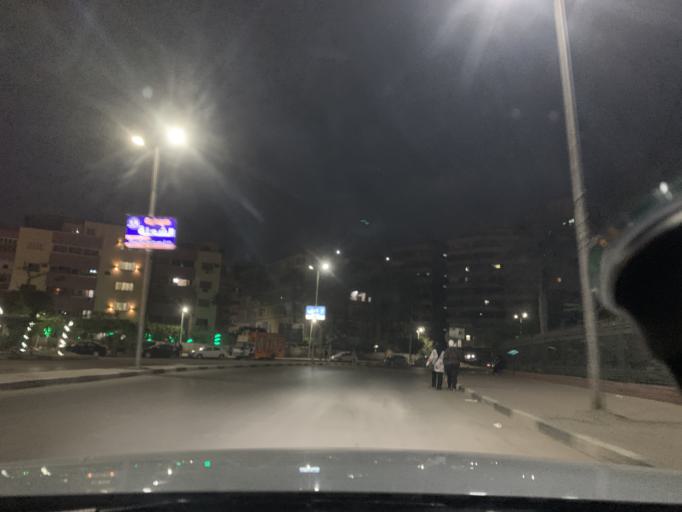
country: EG
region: Muhafazat al Qahirah
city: Cairo
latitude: 30.0890
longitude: 31.2908
